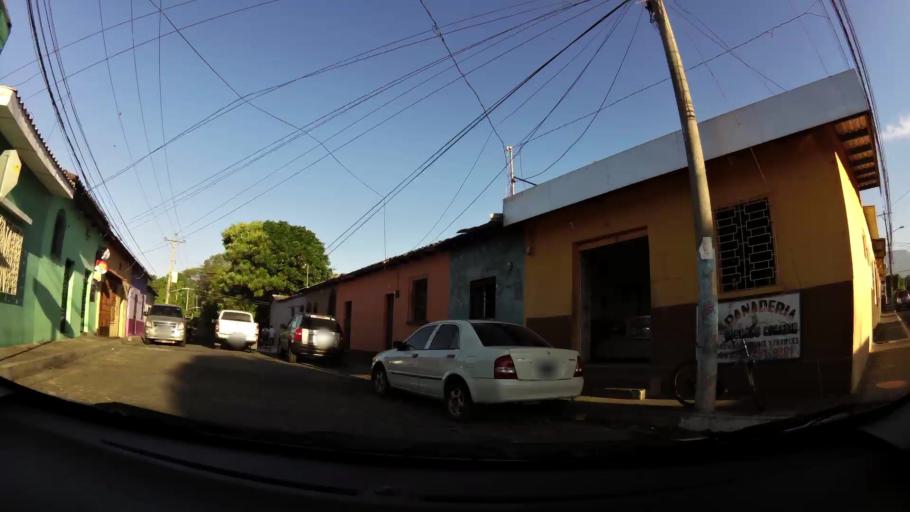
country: SV
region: Sonsonate
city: Sonsonate
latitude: 13.7262
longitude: -89.7227
